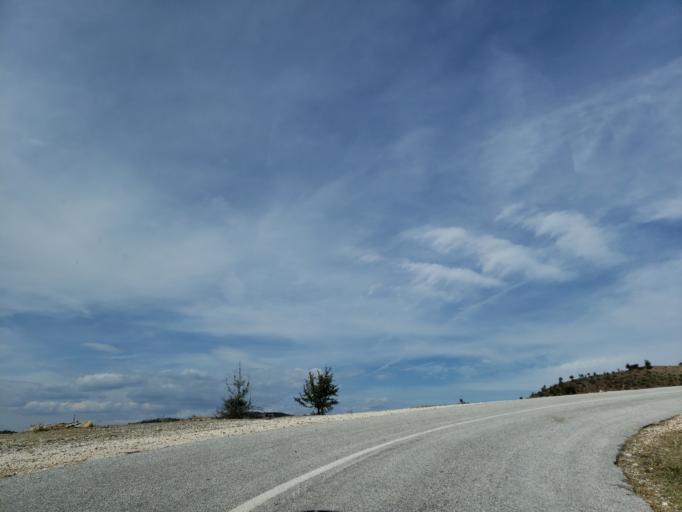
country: GR
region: Thessaly
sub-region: Trikala
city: Kastraki
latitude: 39.7485
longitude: 21.6598
